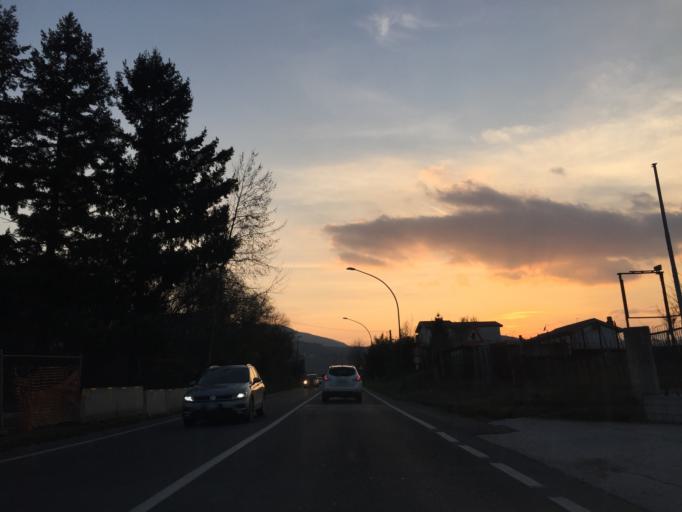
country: IT
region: Campania
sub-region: Provincia di Avellino
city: Avellino
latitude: 40.9021
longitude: 14.8038
